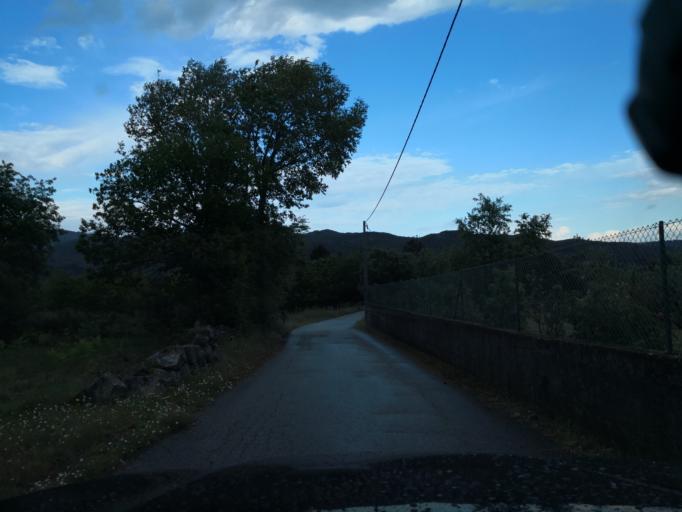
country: PT
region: Vila Real
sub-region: Vila Real
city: Vila Real
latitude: 41.3732
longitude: -7.7155
